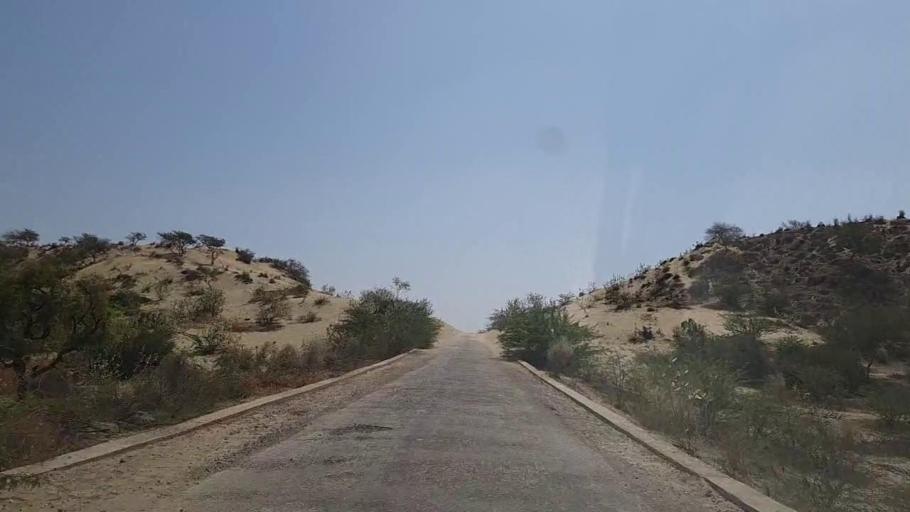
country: PK
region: Sindh
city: Diplo
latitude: 24.5101
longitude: 69.4220
